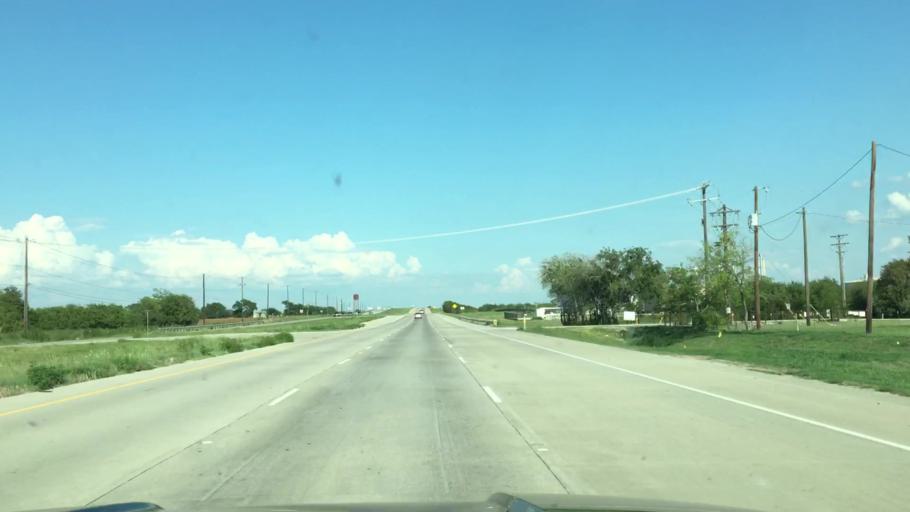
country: US
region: Texas
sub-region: Tarrant County
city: Haslet
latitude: 33.0353
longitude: -97.3511
